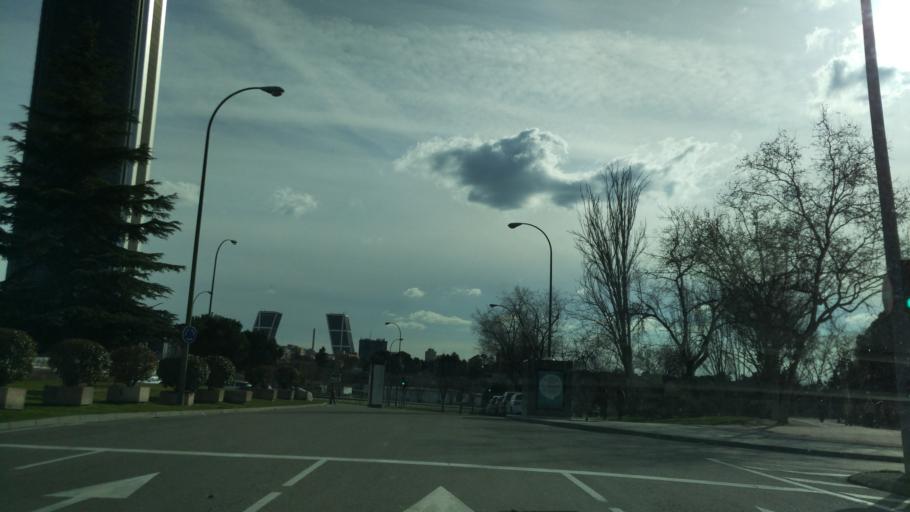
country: ES
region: Madrid
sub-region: Provincia de Madrid
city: Pinar de Chamartin
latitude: 40.4807
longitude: -3.6894
